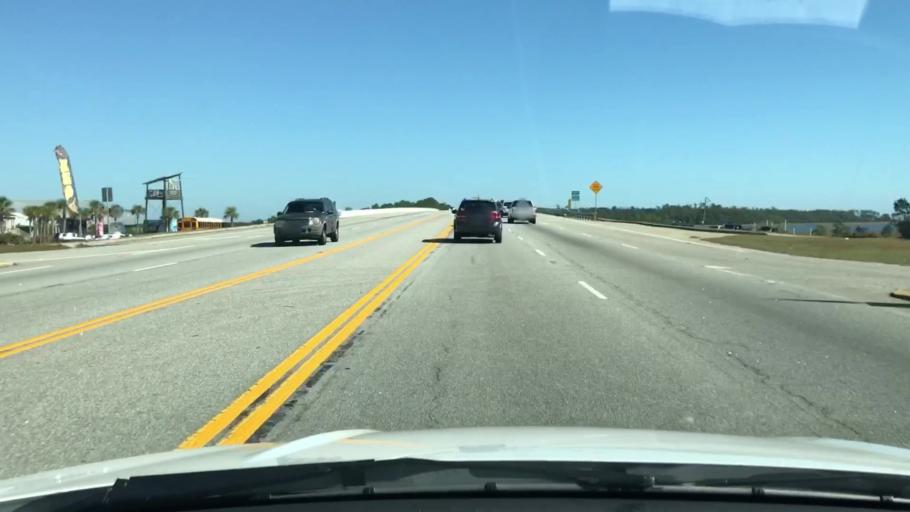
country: US
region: South Carolina
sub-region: Beaufort County
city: Laurel Bay
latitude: 32.3739
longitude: -80.8390
